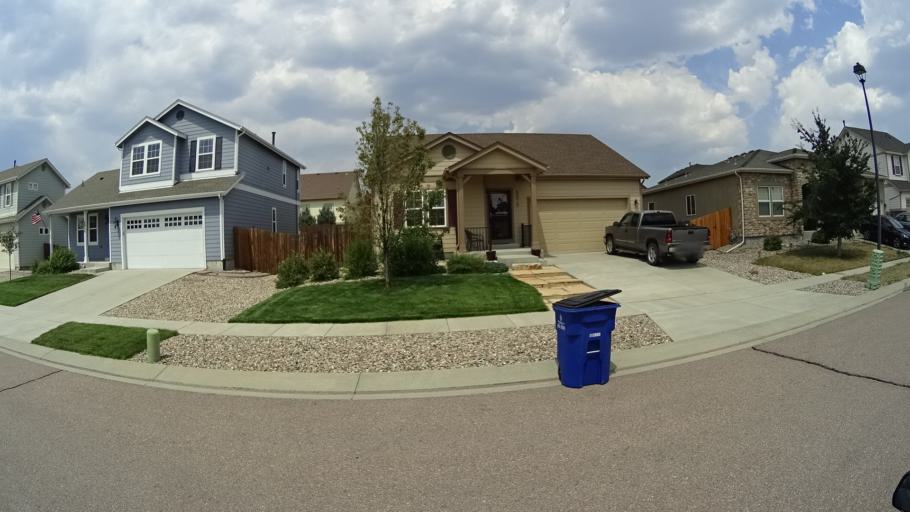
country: US
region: Colorado
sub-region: El Paso County
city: Black Forest
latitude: 38.9502
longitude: -104.6989
